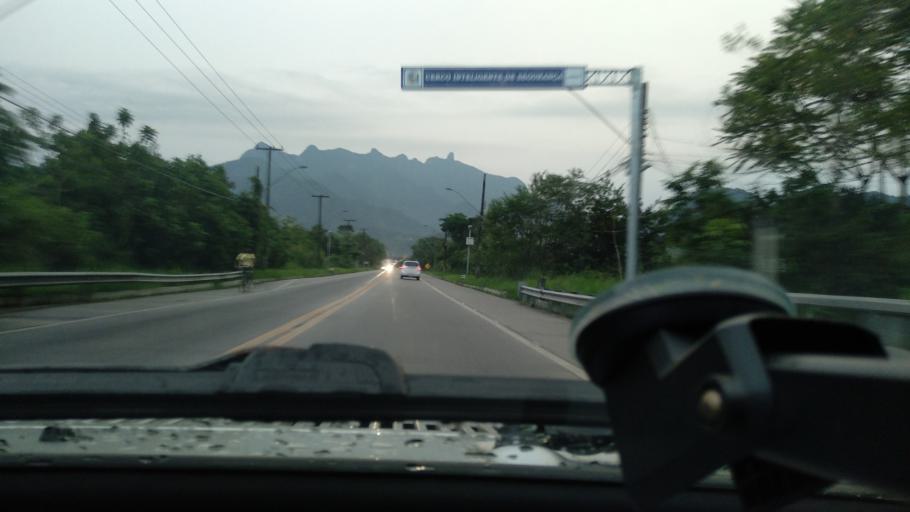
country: BR
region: Rio de Janeiro
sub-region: Angra Dos Reis
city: Angra dos Reis
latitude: -23.0243
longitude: -44.5372
